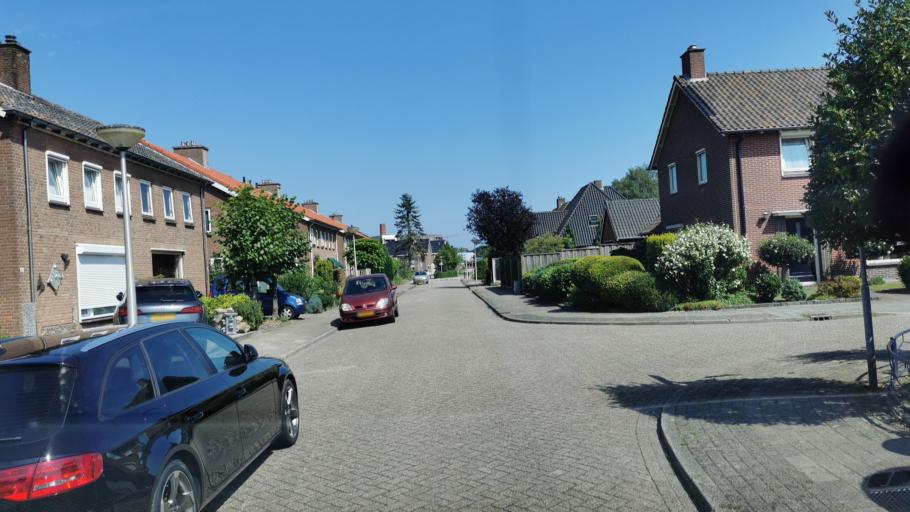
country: NL
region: Overijssel
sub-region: Gemeente Haaksbergen
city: Haaksbergen
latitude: 52.1545
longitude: 6.7340
